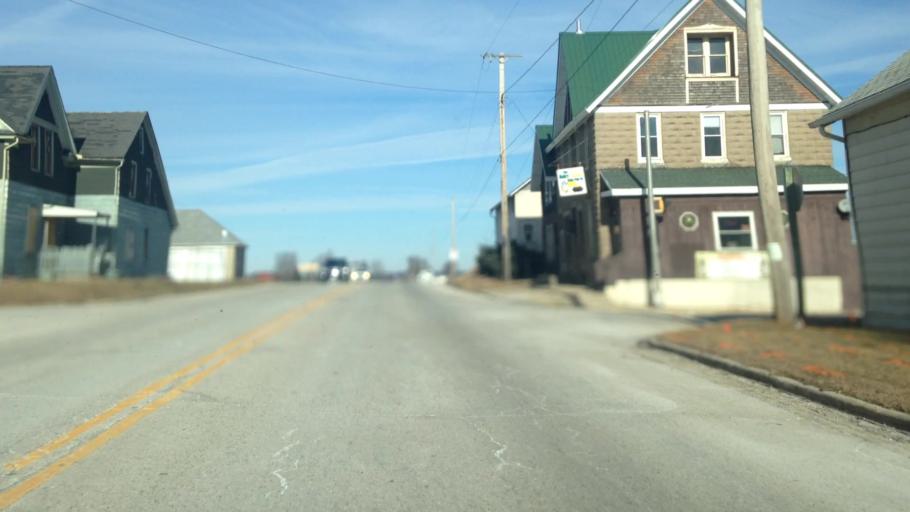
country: US
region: Wisconsin
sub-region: Washington County
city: Richfield
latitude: 43.2656
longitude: -88.2616
